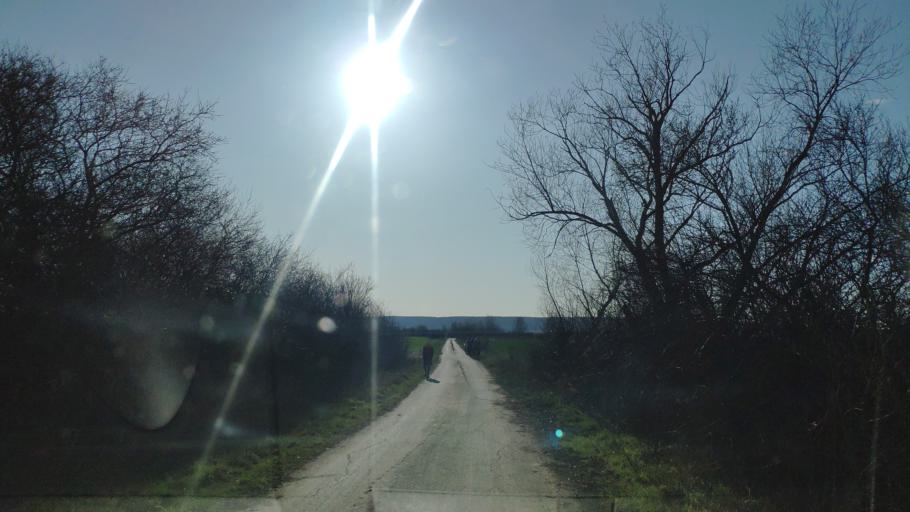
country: SK
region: Kosicky
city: Kosice
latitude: 48.6536
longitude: 21.2480
